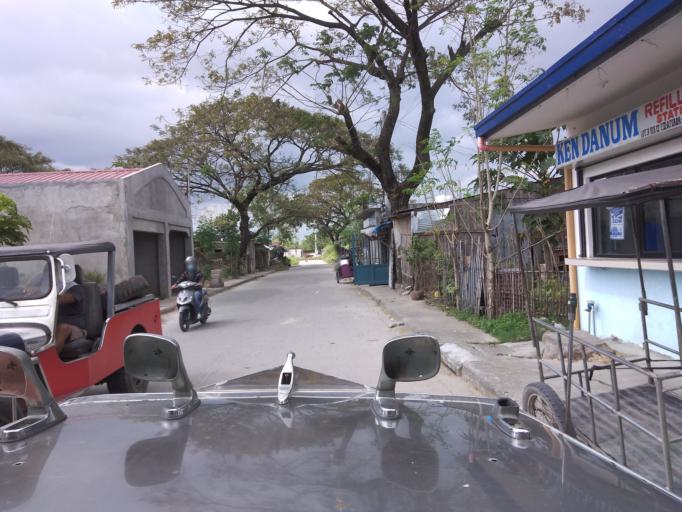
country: PH
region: Central Luzon
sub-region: Province of Pampanga
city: Pandacaqui
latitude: 15.1845
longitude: 120.6473
